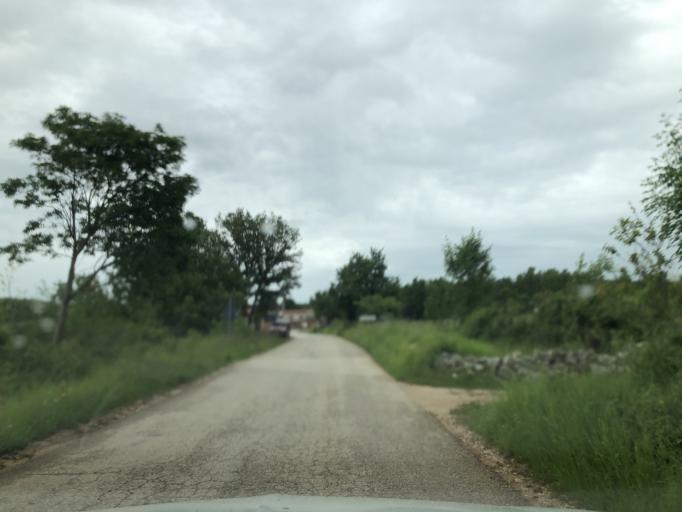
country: HR
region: Istarska
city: Buje
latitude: 45.4306
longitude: 13.6866
